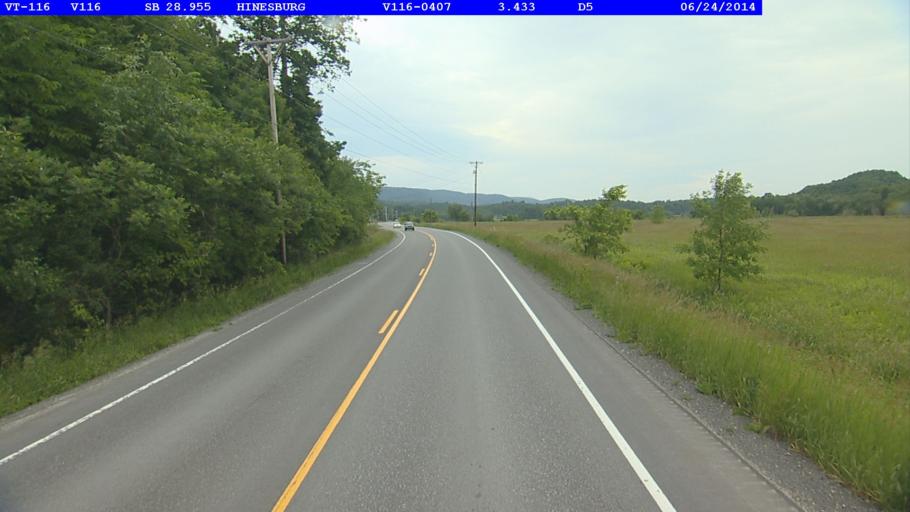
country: US
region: Vermont
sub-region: Chittenden County
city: Hinesburg
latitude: 44.3198
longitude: -73.0953
